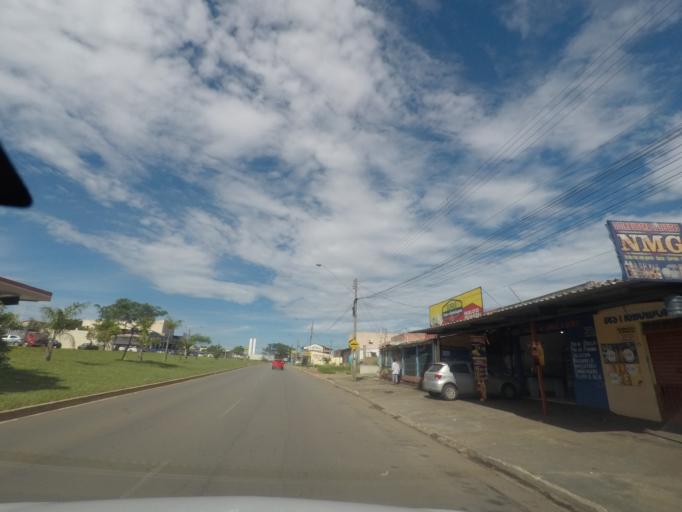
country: BR
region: Goias
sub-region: Aparecida De Goiania
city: Aparecida de Goiania
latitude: -16.7966
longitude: -49.2819
